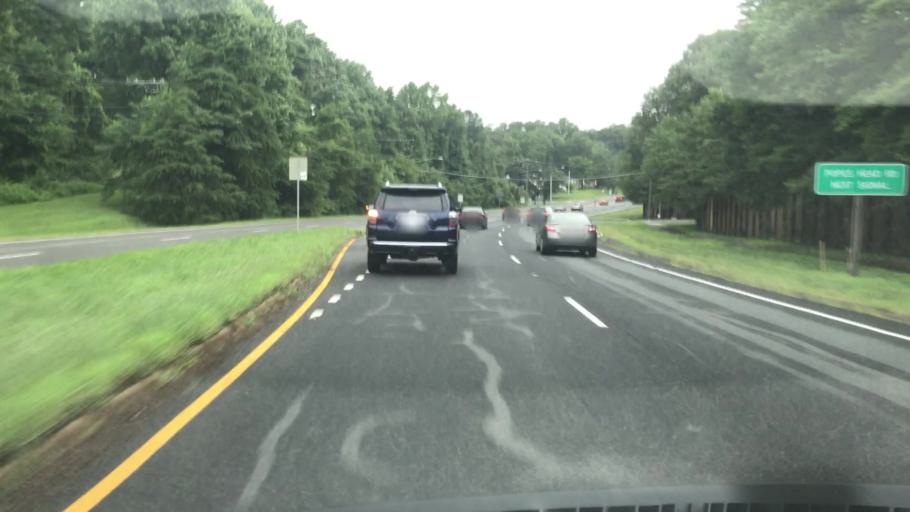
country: US
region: Virginia
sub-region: Fairfax County
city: Fairfax Station
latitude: 38.8105
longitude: -77.3257
